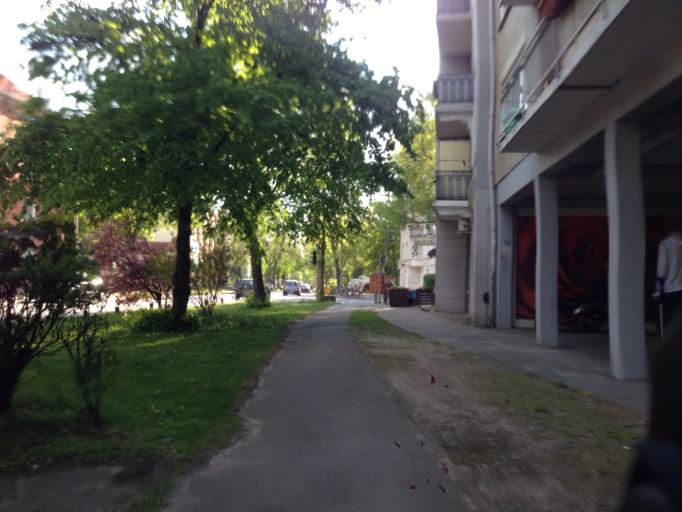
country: DE
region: Hamburg
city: Hamburg
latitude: 53.5780
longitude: 10.0282
